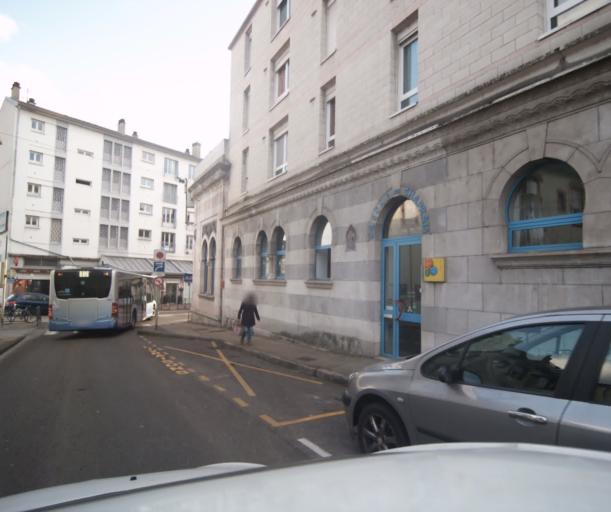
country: FR
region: Franche-Comte
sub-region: Departement du Doubs
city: Besancon
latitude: 47.2483
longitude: 6.0317
